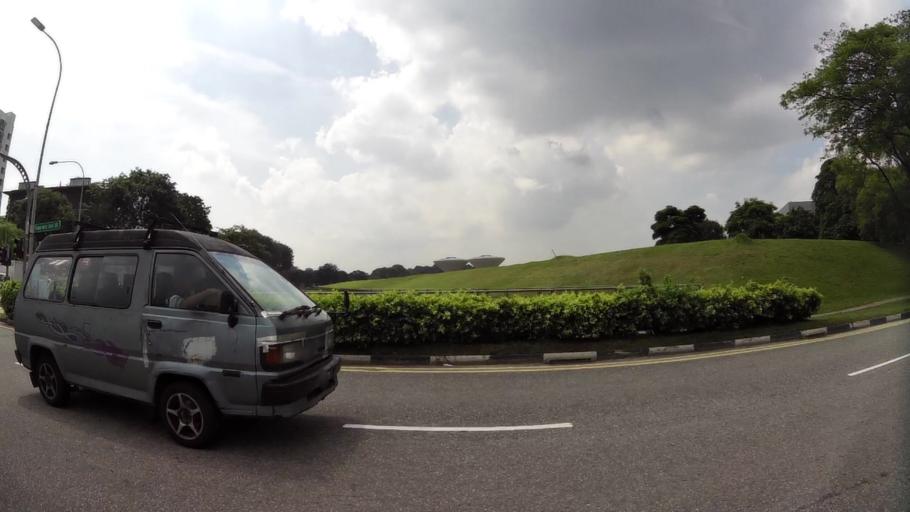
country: SG
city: Singapore
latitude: 1.3692
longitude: 103.9306
